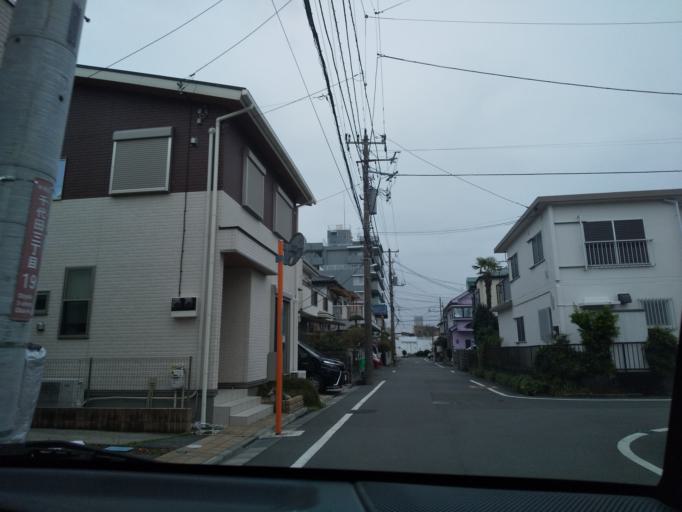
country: JP
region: Kanagawa
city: Zama
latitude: 35.5651
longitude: 139.3779
